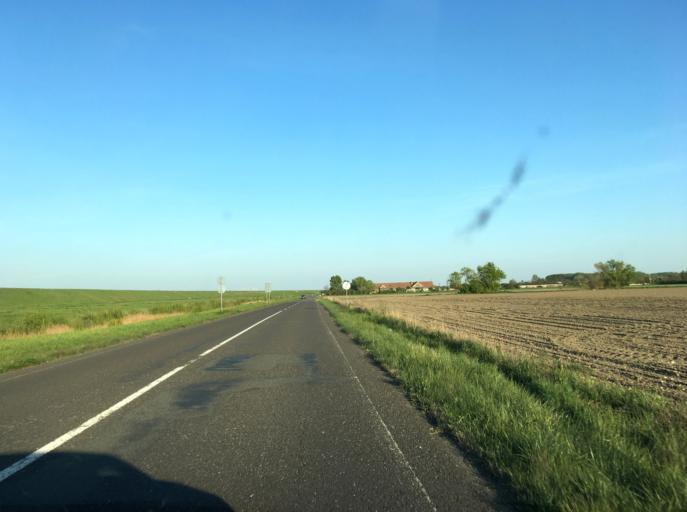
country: SK
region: Trnavsky
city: Samorin
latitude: 47.9908
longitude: 17.3555
